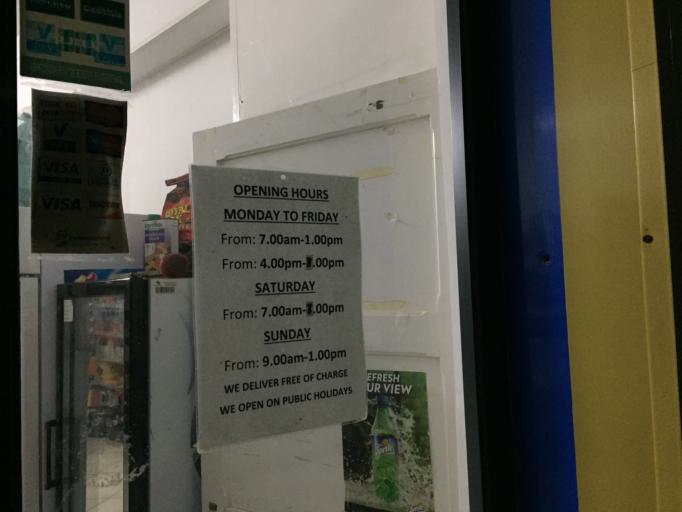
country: MT
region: Ix-Xaghra
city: Xaghra
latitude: 36.0594
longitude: 14.2680
